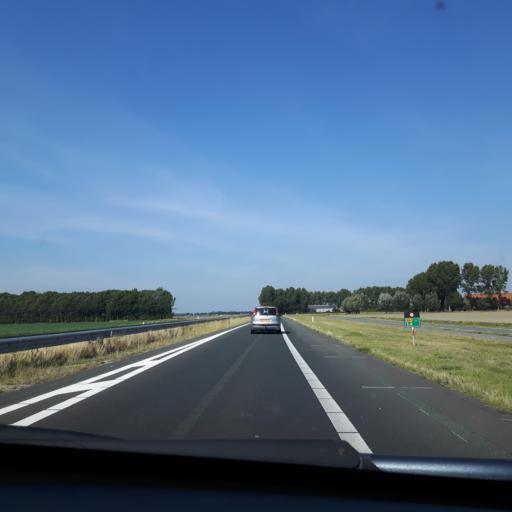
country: BE
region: Flanders
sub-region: Provincie Oost-Vlaanderen
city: Sint-Laureins
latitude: 51.3248
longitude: 3.5947
